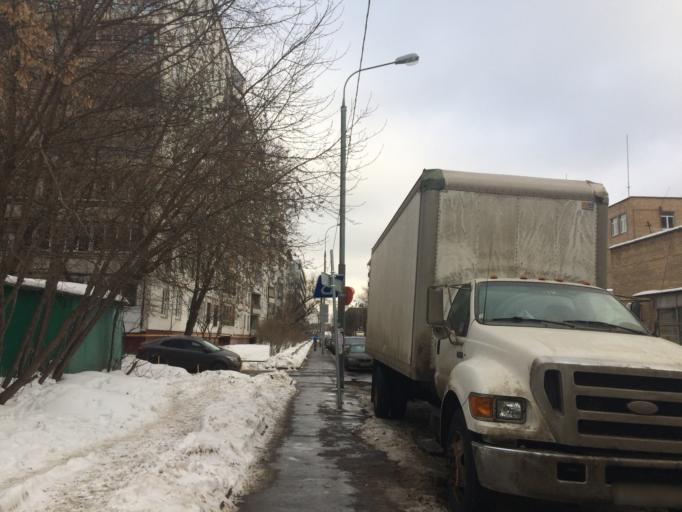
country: RU
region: Moscow
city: Sokol
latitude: 55.8015
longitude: 37.5515
